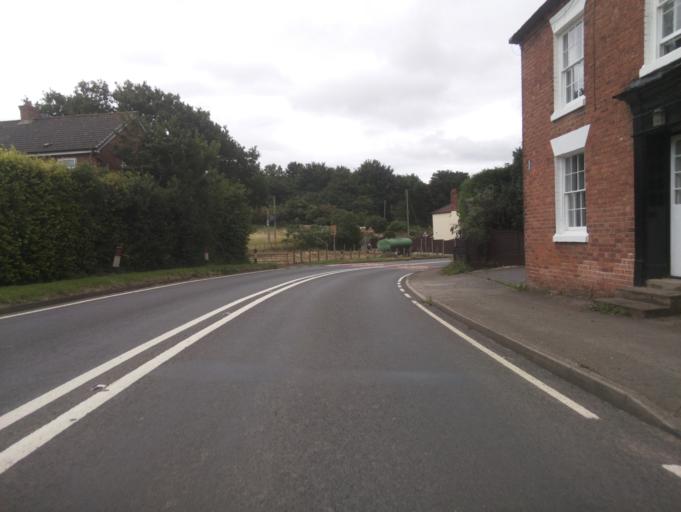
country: GB
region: England
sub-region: Worcestershire
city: Upton upon Severn
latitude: 52.0974
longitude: -2.2088
